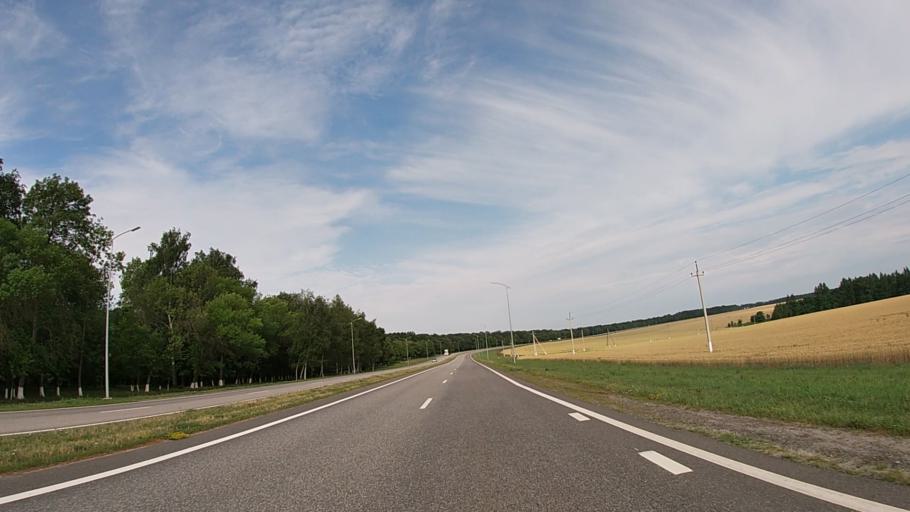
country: RU
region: Belgorod
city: Borisovka
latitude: 50.7511
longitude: 35.9785
